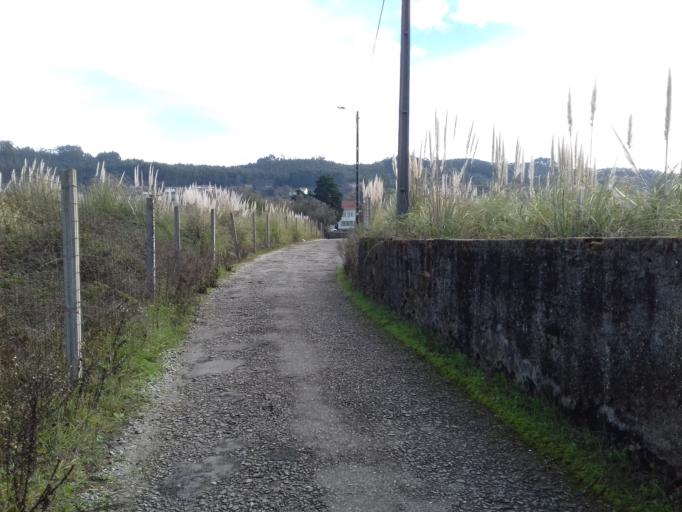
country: PT
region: Aveiro
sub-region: Albergaria-A-Velha
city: Branca
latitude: 40.7646
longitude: -8.4844
